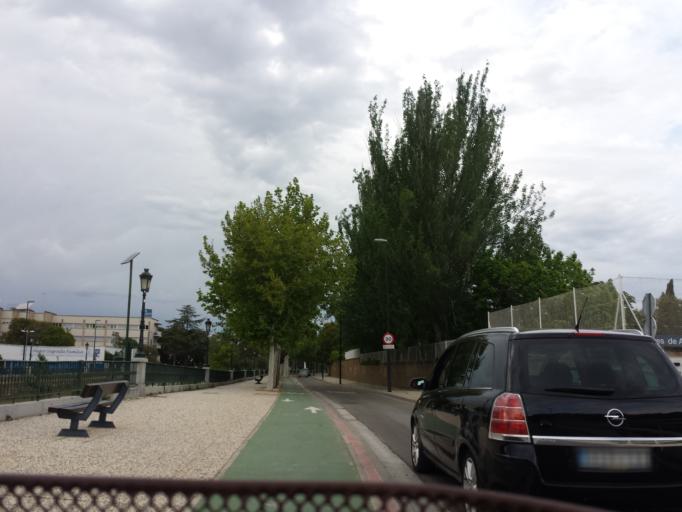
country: ES
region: Aragon
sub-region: Provincia de Zaragoza
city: Delicias
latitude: 41.6226
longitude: -0.9051
